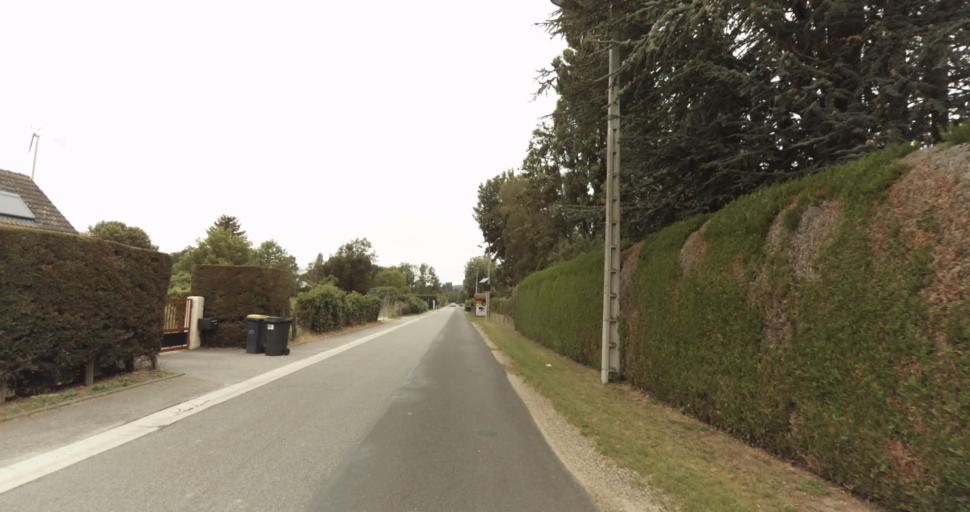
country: FR
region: Haute-Normandie
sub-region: Departement de l'Eure
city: Marcilly-sur-Eure
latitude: 48.8211
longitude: 1.3561
